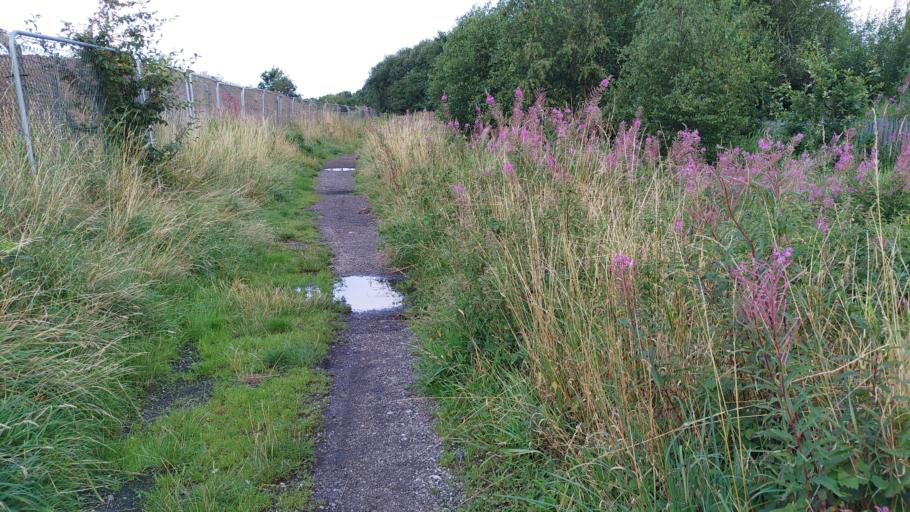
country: GB
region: England
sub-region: Lancashire
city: Coppull
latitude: 53.6282
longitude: -2.6614
